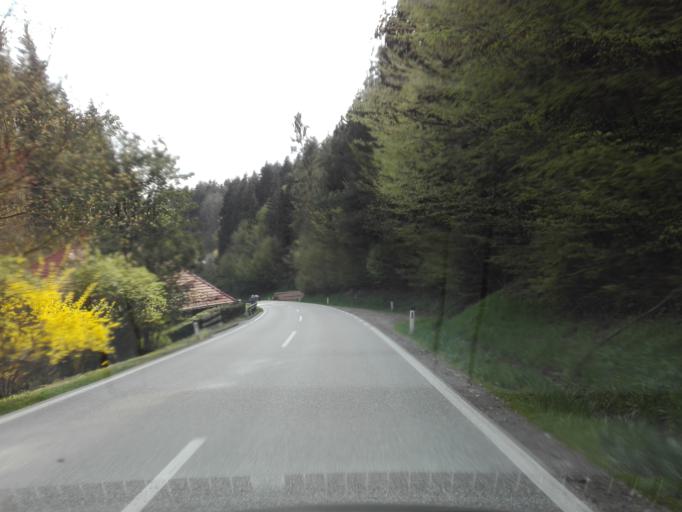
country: AT
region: Upper Austria
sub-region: Politischer Bezirk Urfahr-Umgebung
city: Feldkirchen an der Donau
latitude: 48.3815
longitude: 14.0651
